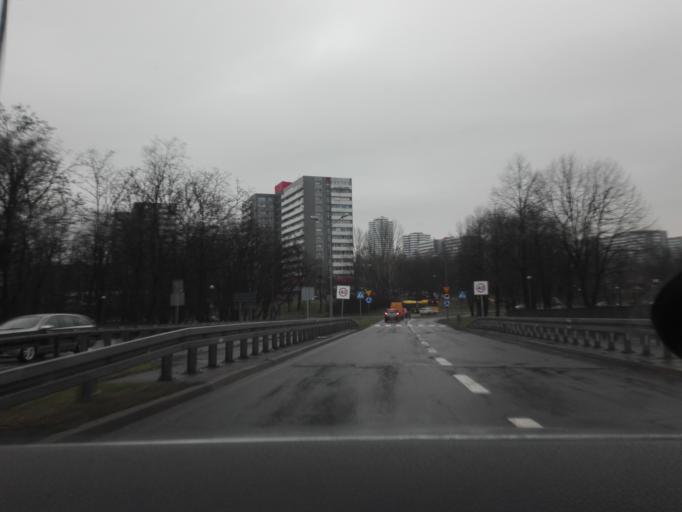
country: PL
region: Silesian Voivodeship
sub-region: Chorzow
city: Chorzow
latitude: 50.2727
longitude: 18.9755
